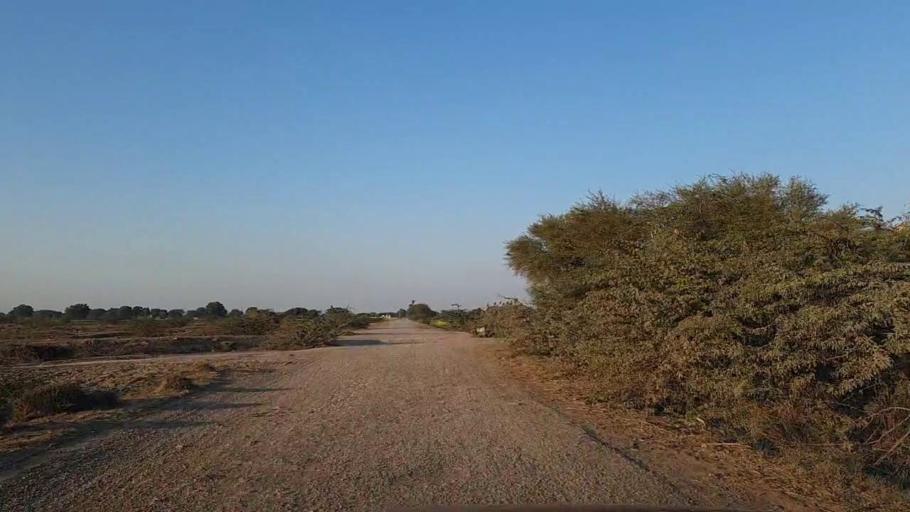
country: PK
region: Sindh
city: Nawabshah
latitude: 26.2224
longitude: 68.3379
